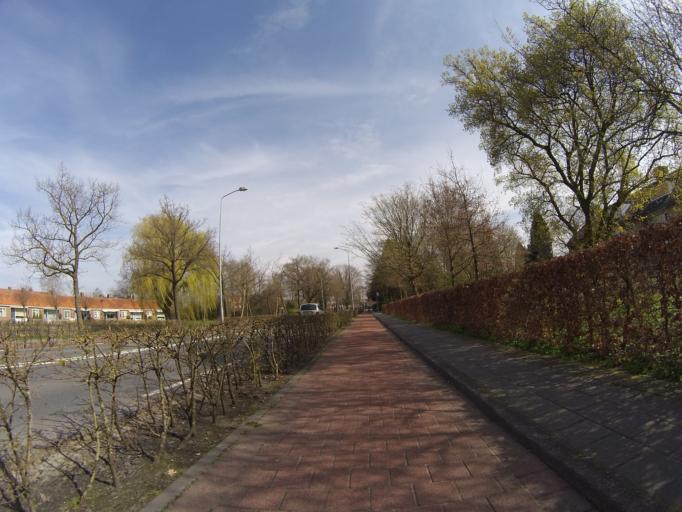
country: NL
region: Gelderland
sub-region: Gemeente Nijkerk
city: Nijkerk
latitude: 52.2179
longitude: 5.4787
